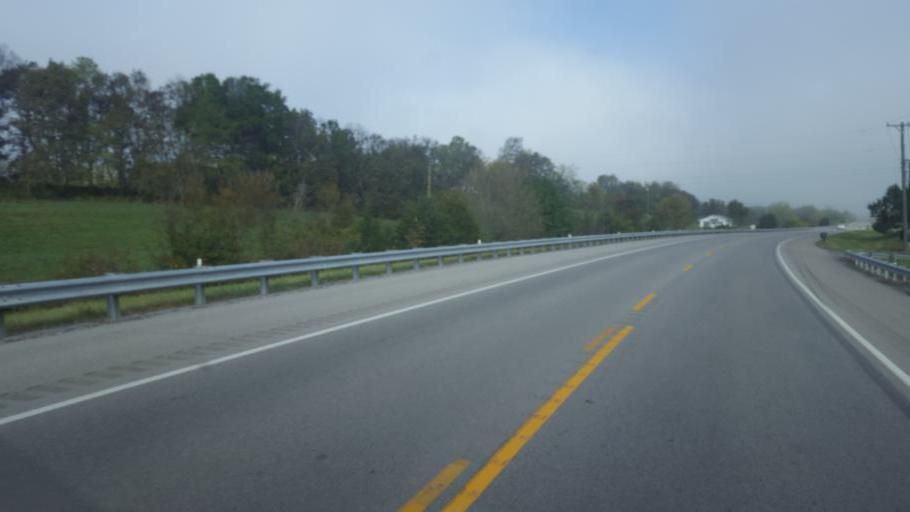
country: US
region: Kentucky
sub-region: Mason County
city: Maysville
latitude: 38.5357
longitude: -83.7591
